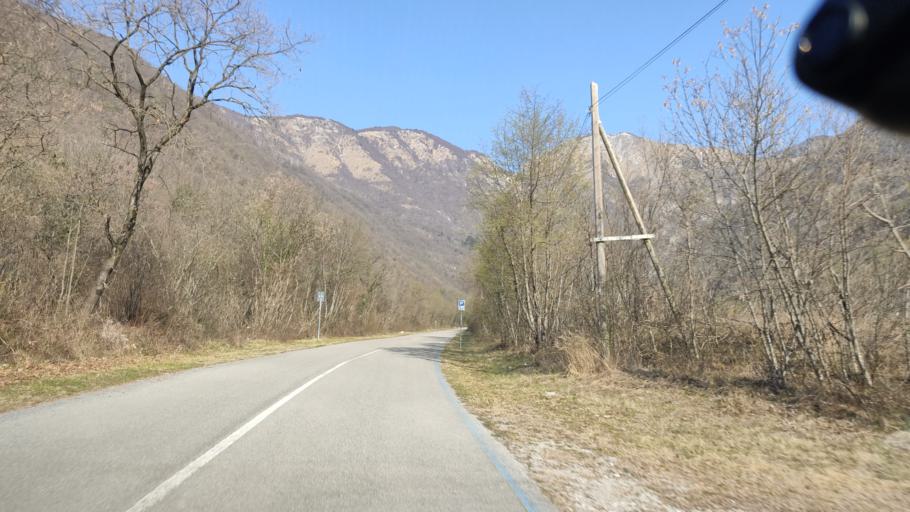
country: IT
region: Friuli Venezia Giulia
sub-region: Provincia di Pordenone
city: Budoia
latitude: 46.0604
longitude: 12.5199
